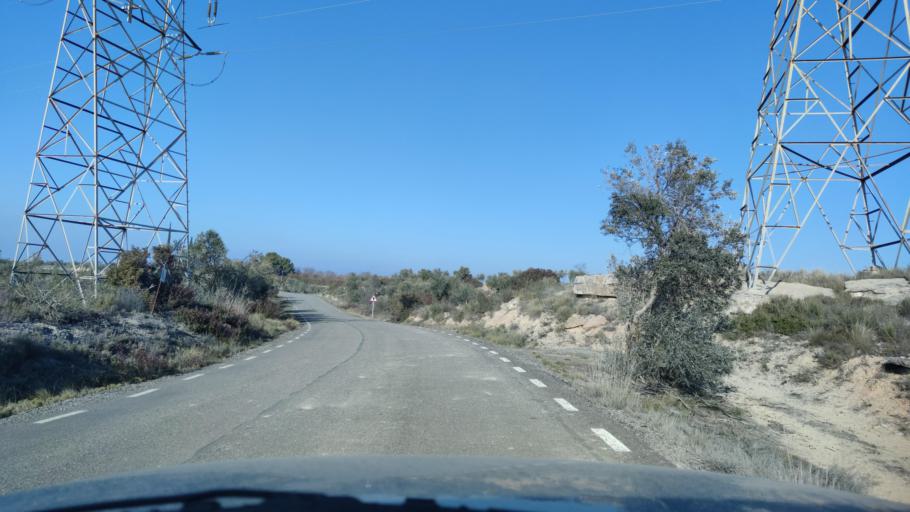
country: ES
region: Catalonia
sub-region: Provincia de Lleida
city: Torrebesses
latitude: 41.4338
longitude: 0.5678
